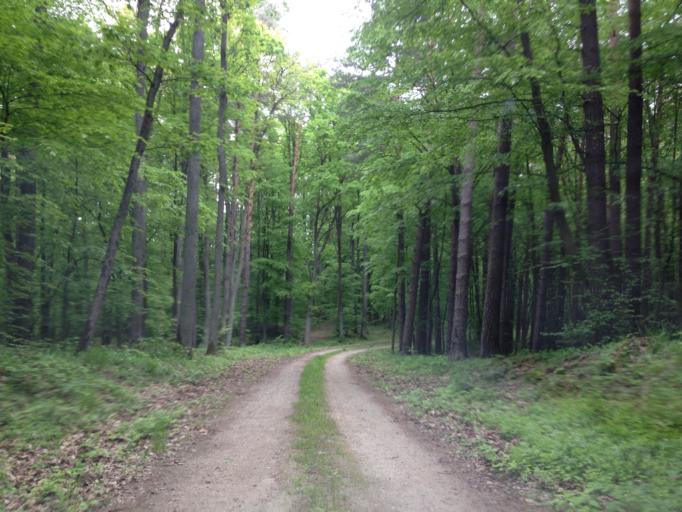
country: PL
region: Kujawsko-Pomorskie
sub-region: Powiat brodnicki
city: Gorzno
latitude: 53.2581
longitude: 19.7103
